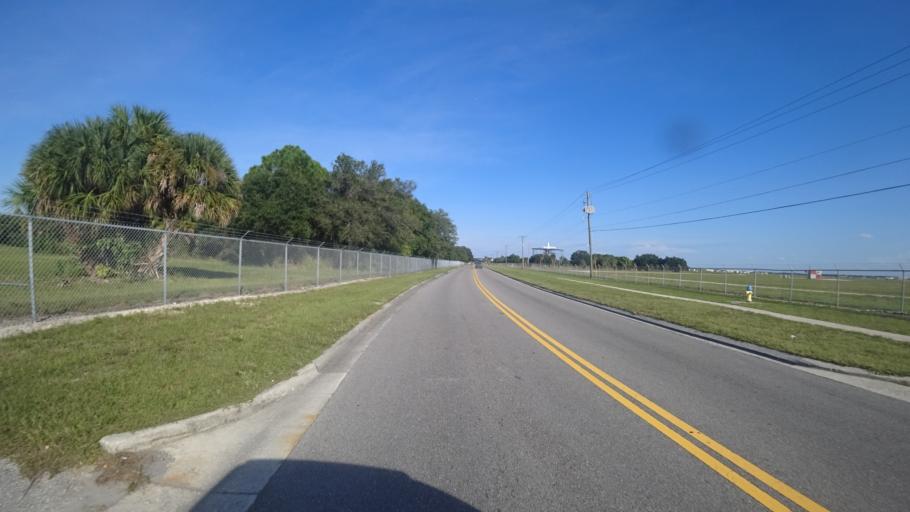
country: US
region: Florida
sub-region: Manatee County
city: Whitfield
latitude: 27.4076
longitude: -82.5671
